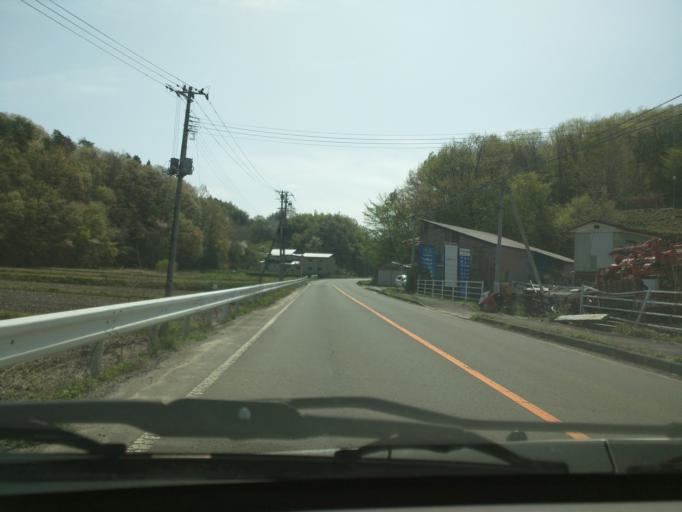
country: JP
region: Fukushima
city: Nihommatsu
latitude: 37.5723
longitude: 140.4840
